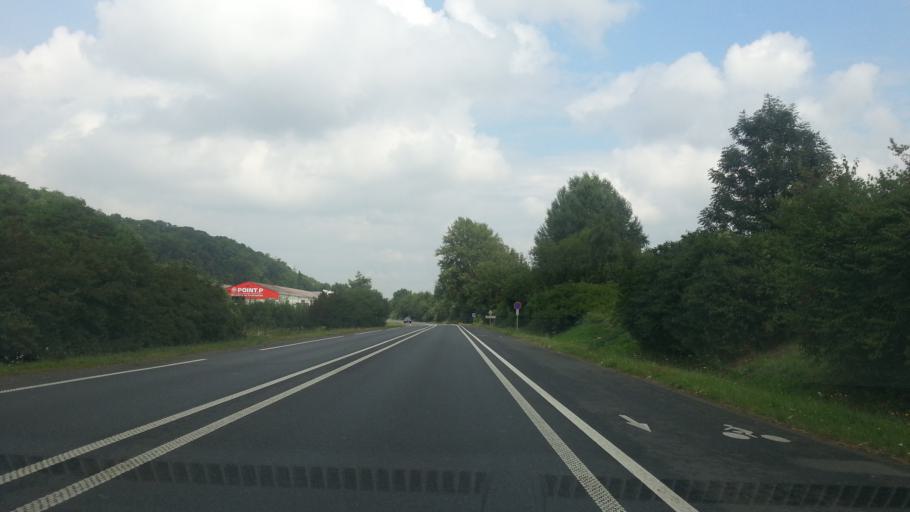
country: FR
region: Picardie
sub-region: Departement de l'Oise
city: Thiverny
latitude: 49.2321
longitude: 2.4347
